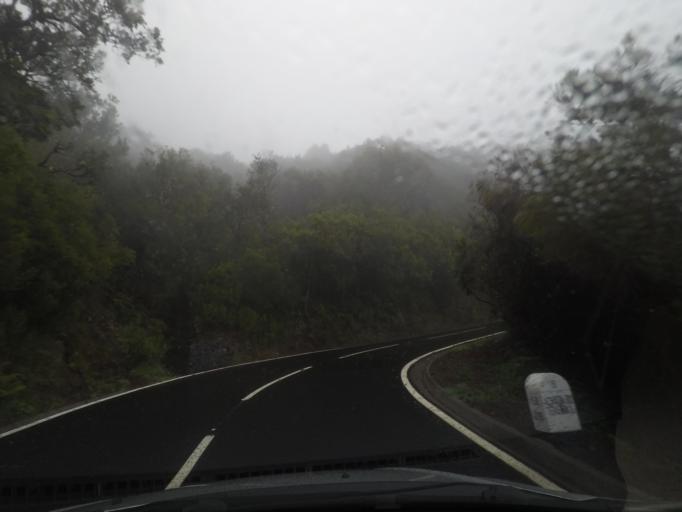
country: PT
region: Madeira
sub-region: Santana
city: Santana
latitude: 32.7680
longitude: -16.9167
